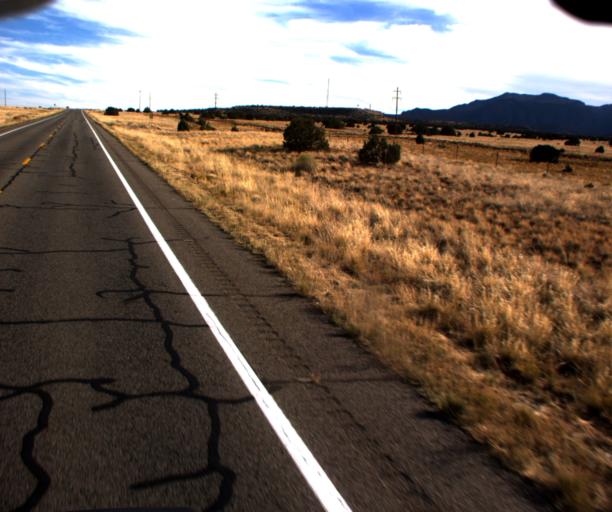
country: US
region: New Mexico
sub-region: San Juan County
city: Shiprock
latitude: 36.8991
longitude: -109.0662
